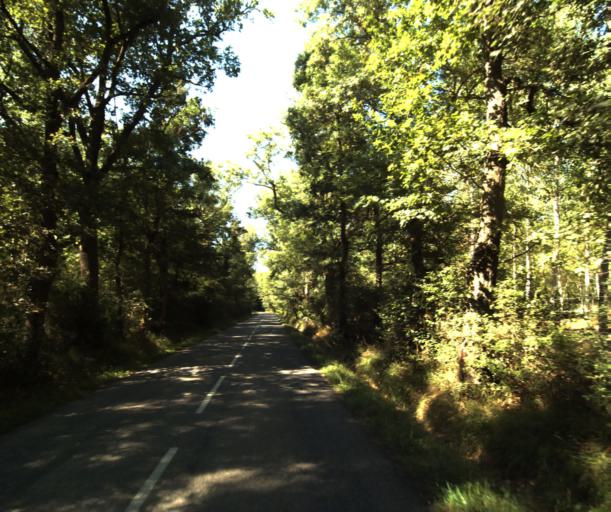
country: FR
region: Midi-Pyrenees
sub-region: Departement de la Haute-Garonne
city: Fonsorbes
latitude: 43.4957
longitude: 1.2288
